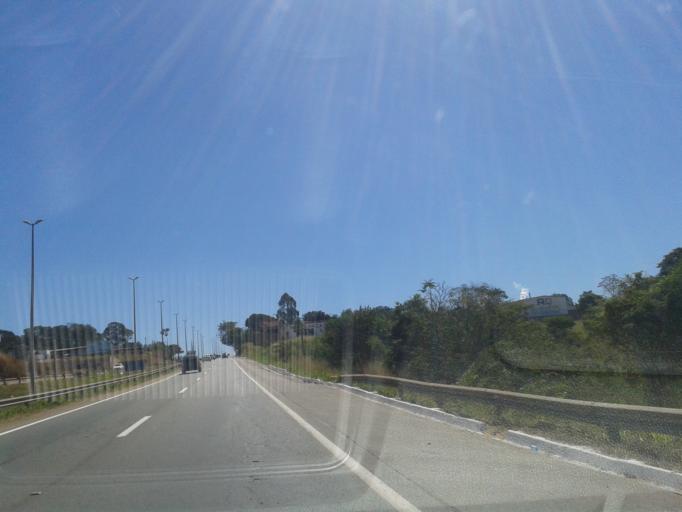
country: BR
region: Goias
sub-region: Goiania
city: Goiania
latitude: -16.6334
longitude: -49.3471
